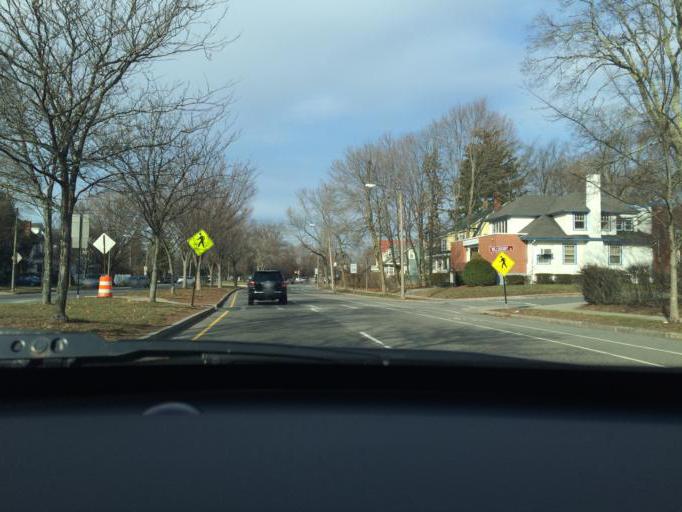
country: US
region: Massachusetts
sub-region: Norfolk County
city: Milton
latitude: 42.2632
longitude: -71.0936
